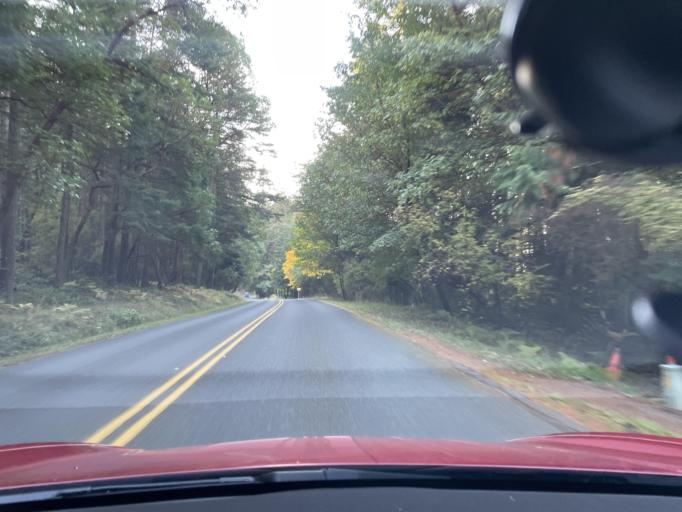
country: US
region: Washington
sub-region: San Juan County
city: Friday Harbor
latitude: 48.5443
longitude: -123.1590
